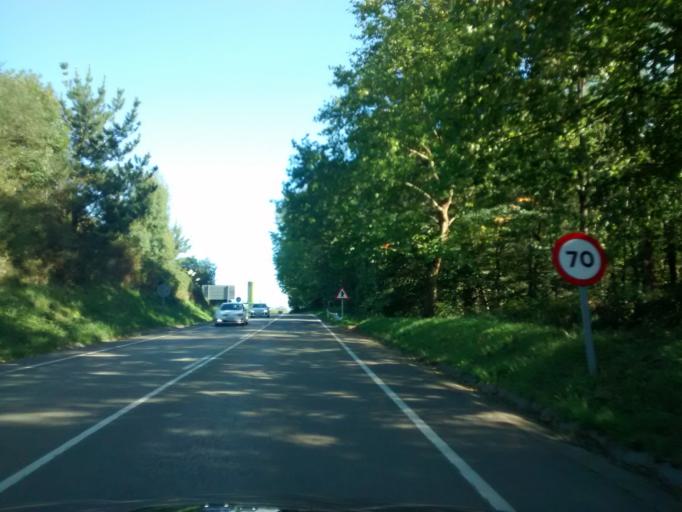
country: ES
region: Cantabria
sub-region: Provincia de Cantabria
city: Cabezon de la Sal
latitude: 43.3196
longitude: -4.2562
